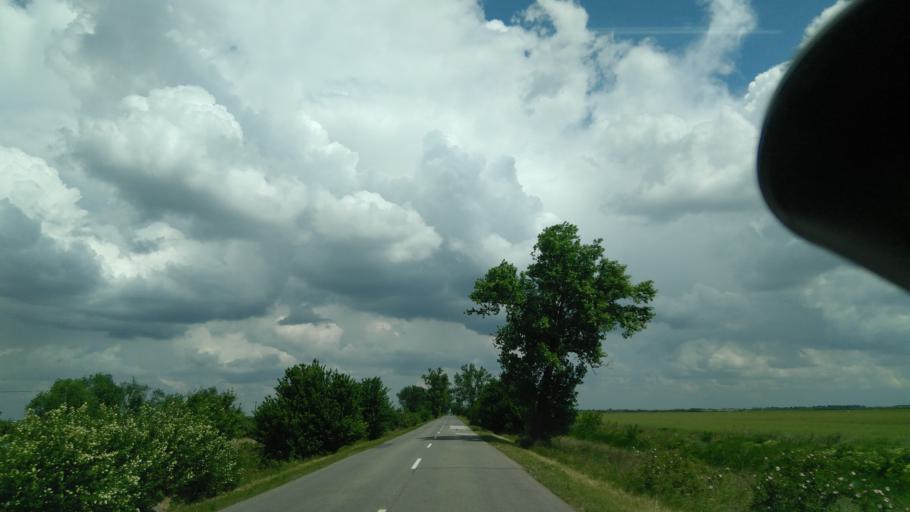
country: HU
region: Bekes
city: Devavanya
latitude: 46.9994
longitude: 20.9107
